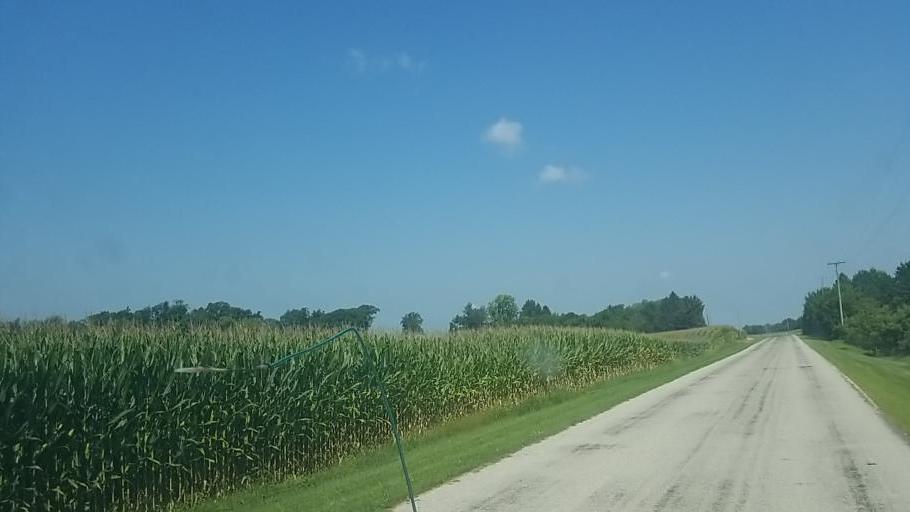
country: US
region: Ohio
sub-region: Marion County
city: Marion
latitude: 40.7002
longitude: -83.1603
